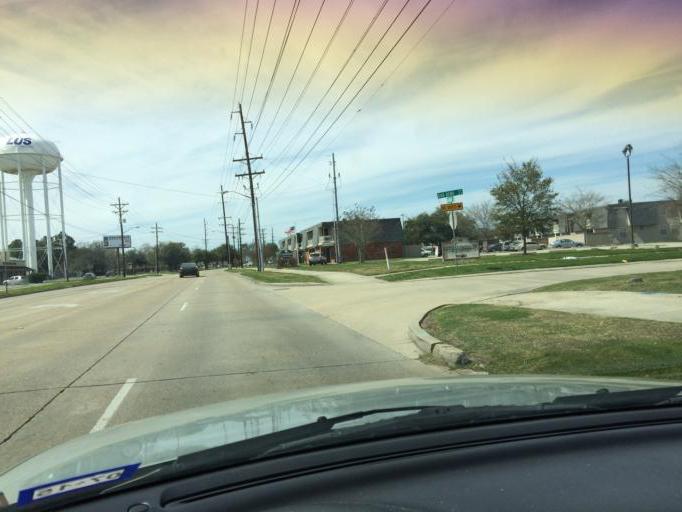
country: US
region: Louisiana
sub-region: Lafayette Parish
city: Scott
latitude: 30.1963
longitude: -92.0660
